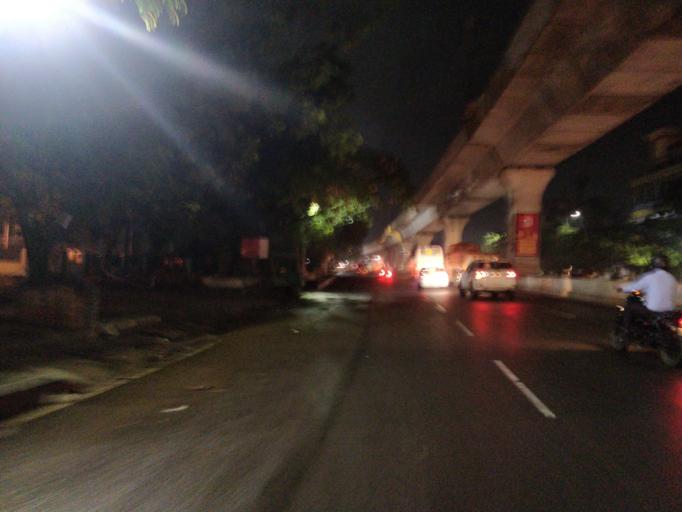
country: IN
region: Telangana
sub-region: Rangareddi
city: Gaddi Annaram
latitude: 17.3718
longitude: 78.5106
